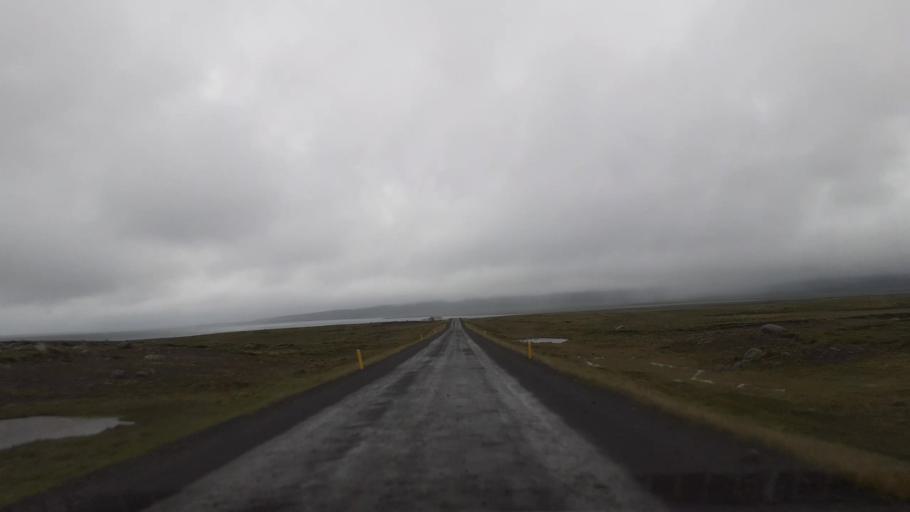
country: IS
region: East
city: Egilsstadir
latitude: 66.0742
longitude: -15.1013
